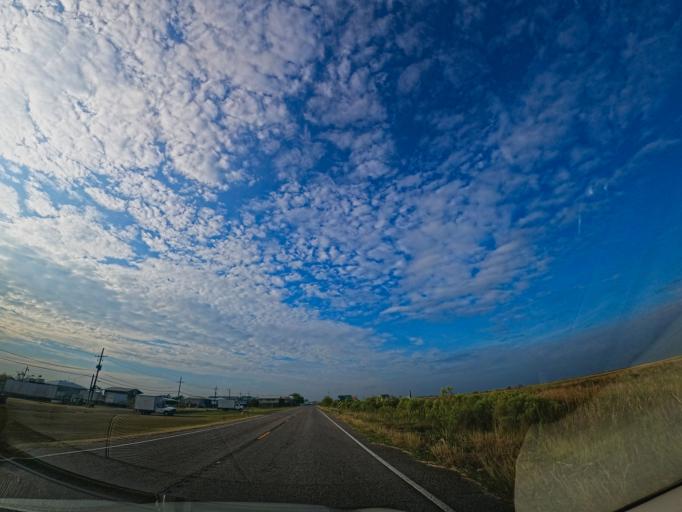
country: US
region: Louisiana
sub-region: Terrebonne Parish
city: Dulac
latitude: 29.3259
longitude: -90.6444
